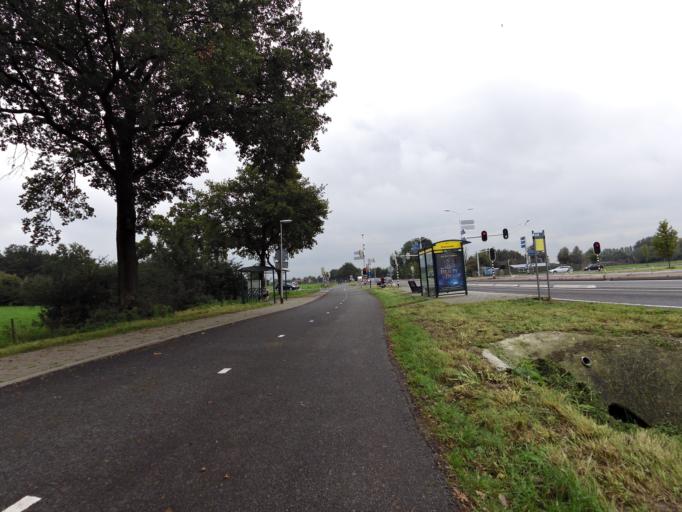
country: NL
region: Gelderland
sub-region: Oude IJsselstreek
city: Gendringen
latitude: 51.9145
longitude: 6.3362
